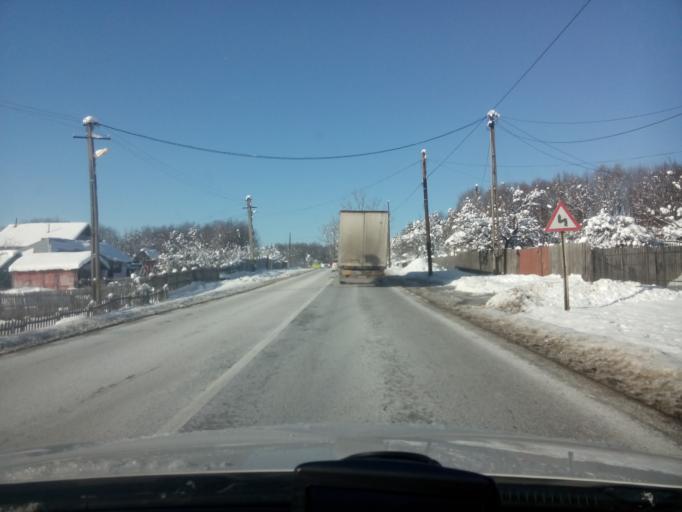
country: RO
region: Arges
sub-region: Comuna Cotmeana
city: Cotmeana
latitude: 44.9884
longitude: 24.6443
